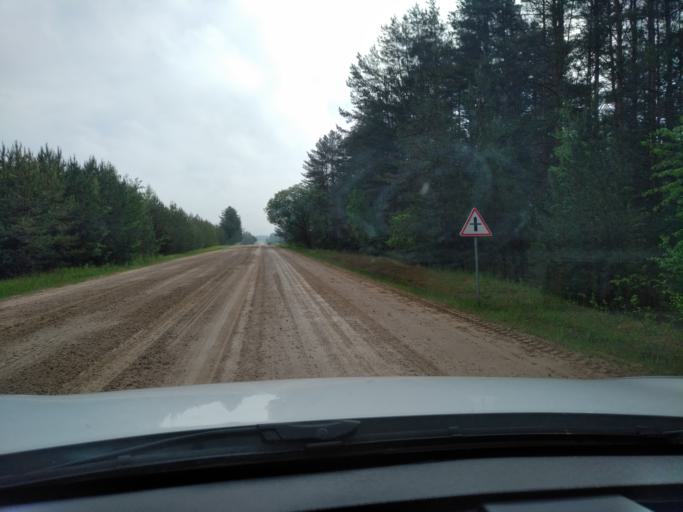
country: LT
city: Svencionys
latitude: 55.2400
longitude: 26.1414
